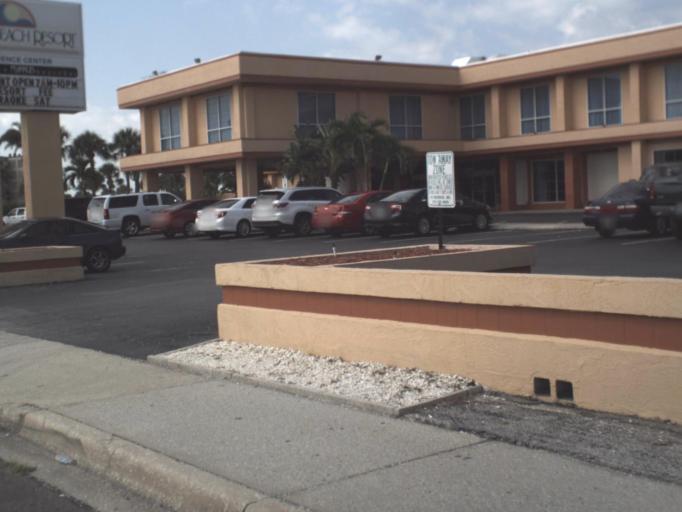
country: US
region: Florida
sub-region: Pinellas County
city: Saint Pete Beach
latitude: 27.7230
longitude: -82.7407
